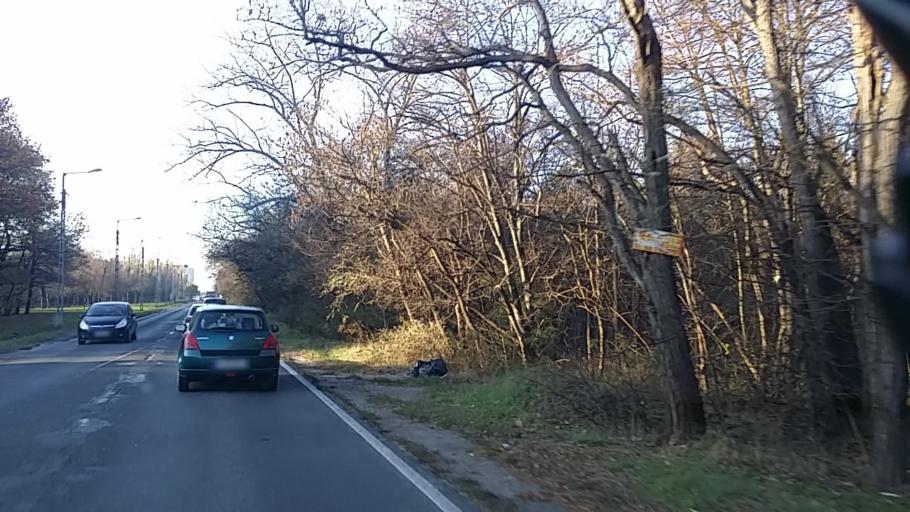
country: HU
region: Budapest
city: Budapest XVI. keruelet
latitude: 47.5431
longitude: 19.1500
